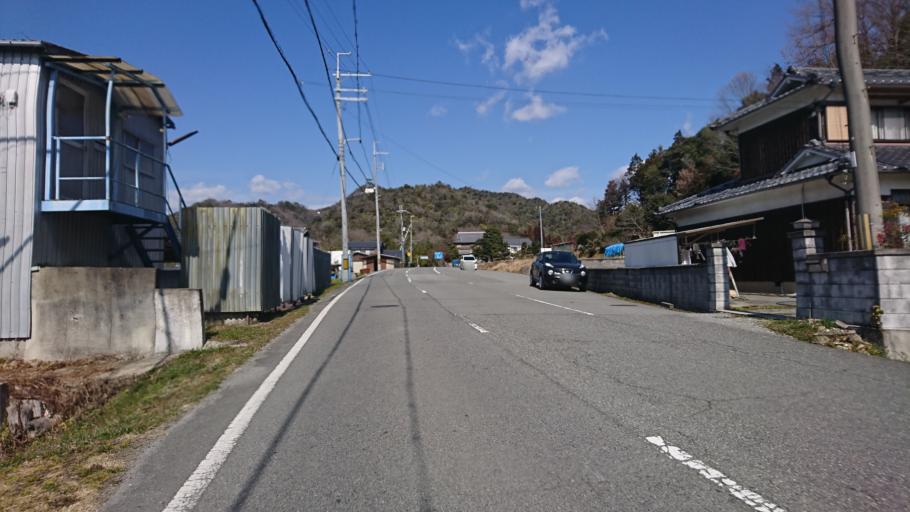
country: JP
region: Hyogo
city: Kakogawacho-honmachi
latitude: 34.8520
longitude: 134.8101
